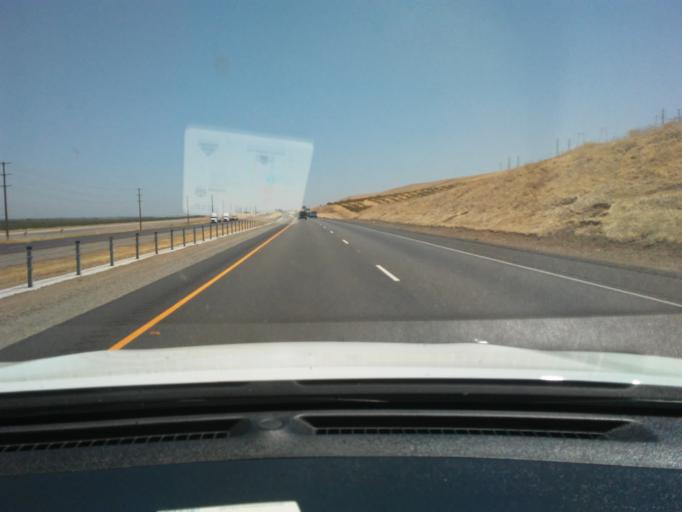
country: US
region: California
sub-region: Stanislaus County
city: Patterson
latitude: 37.5045
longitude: -121.2253
